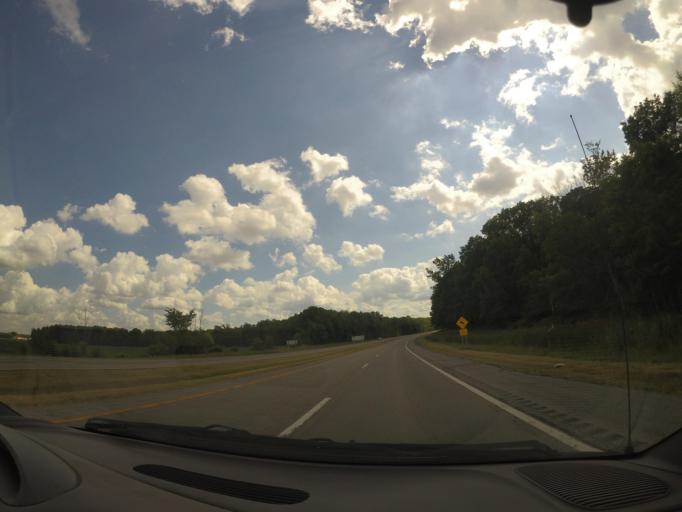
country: US
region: Ohio
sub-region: Huron County
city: Norwalk
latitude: 41.2311
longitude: -82.5750
